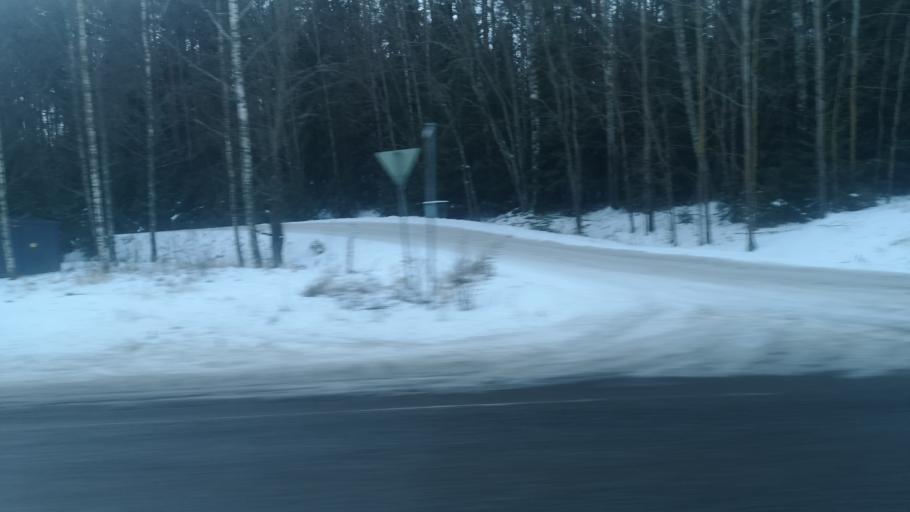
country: FI
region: Varsinais-Suomi
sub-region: Salo
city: Salo
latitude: 60.3621
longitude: 23.1816
